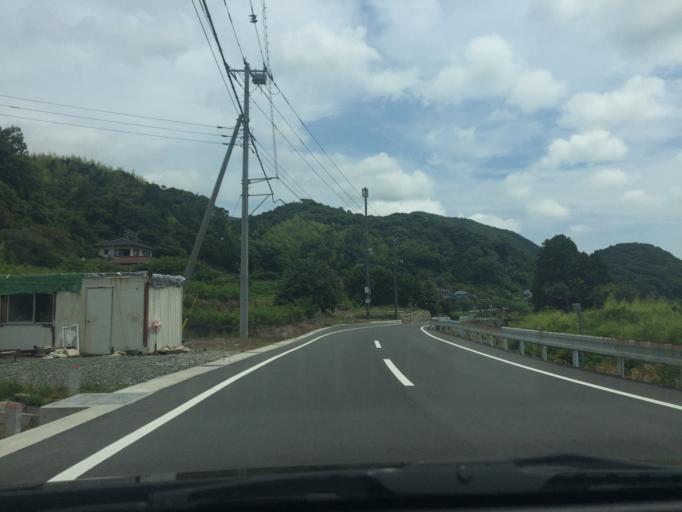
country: JP
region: Shizuoka
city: Shimoda
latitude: 34.6847
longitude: 138.8191
